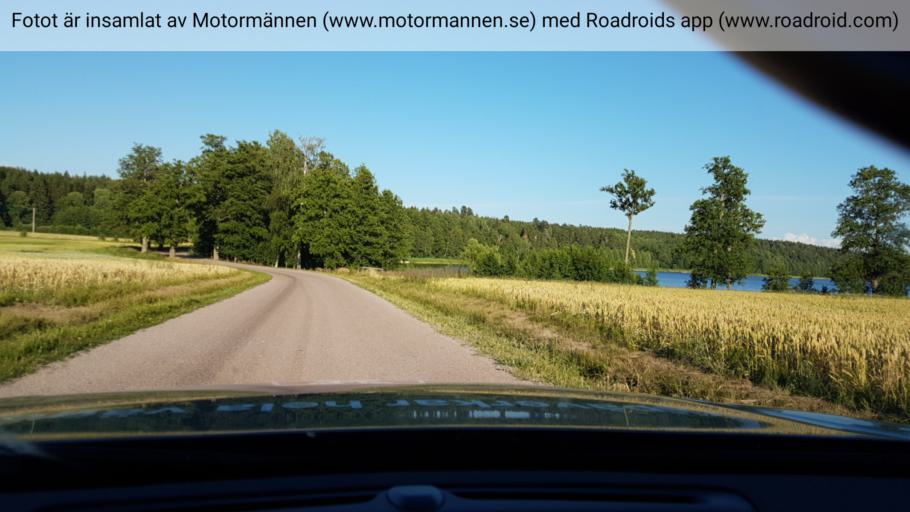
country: SE
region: Vaestmanland
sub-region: Surahammars Kommun
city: Ramnas
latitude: 59.6945
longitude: 16.0704
